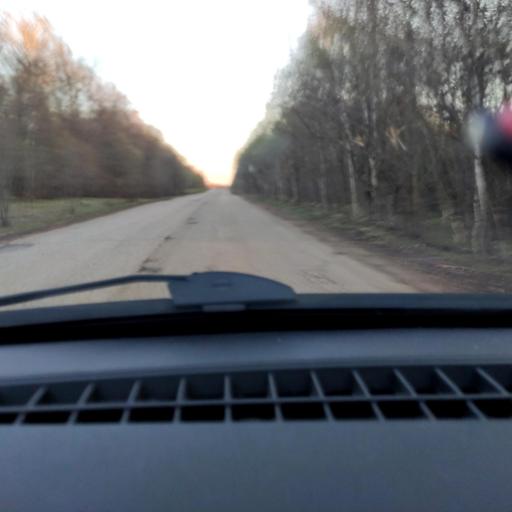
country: RU
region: Bashkortostan
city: Chishmy
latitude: 54.4512
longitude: 55.5478
